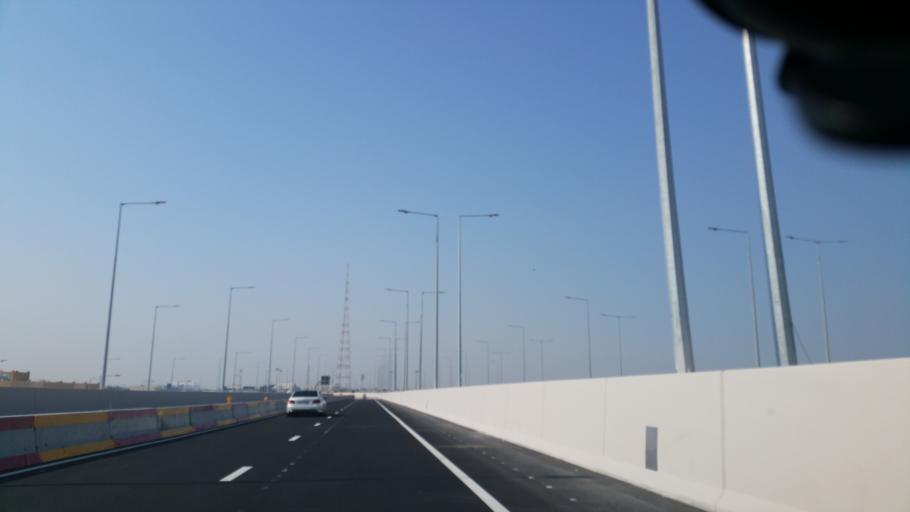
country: QA
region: Baladiyat ad Dawhah
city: Doha
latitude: 25.2737
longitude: 51.4742
